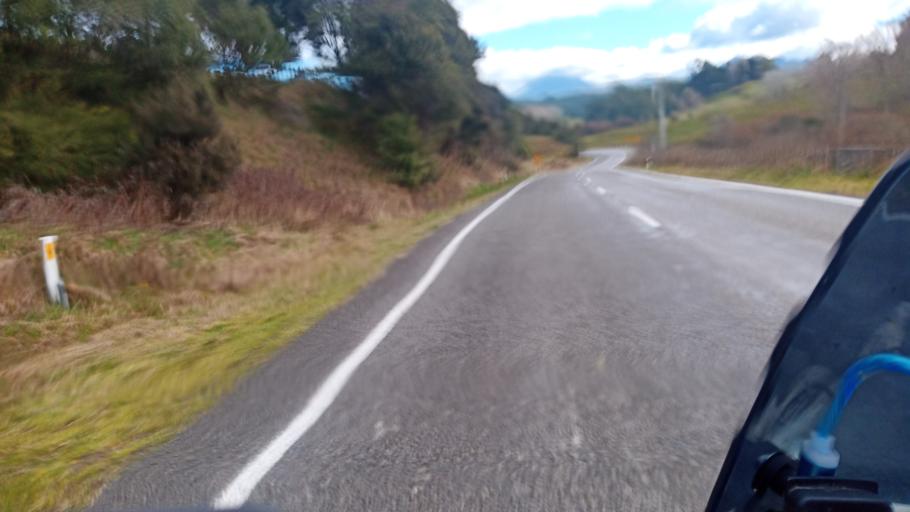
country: NZ
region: Gisborne
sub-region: Gisborne District
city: Gisborne
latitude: -38.0299
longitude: 178.2810
